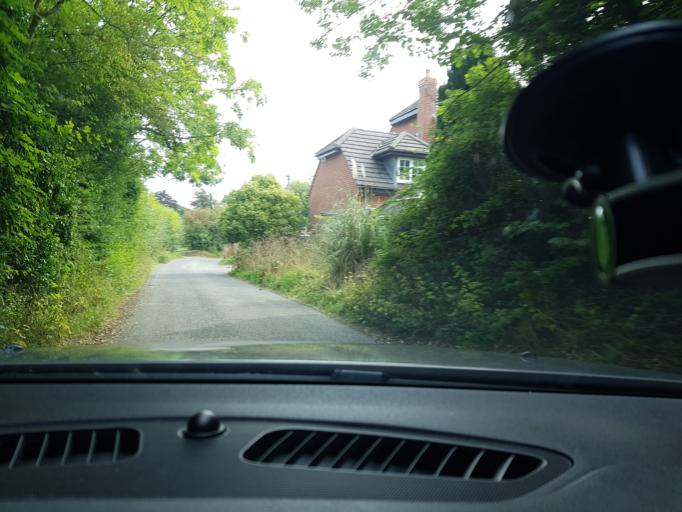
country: GB
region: England
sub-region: West Berkshire
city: Hungerford
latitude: 51.4140
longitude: -1.5282
